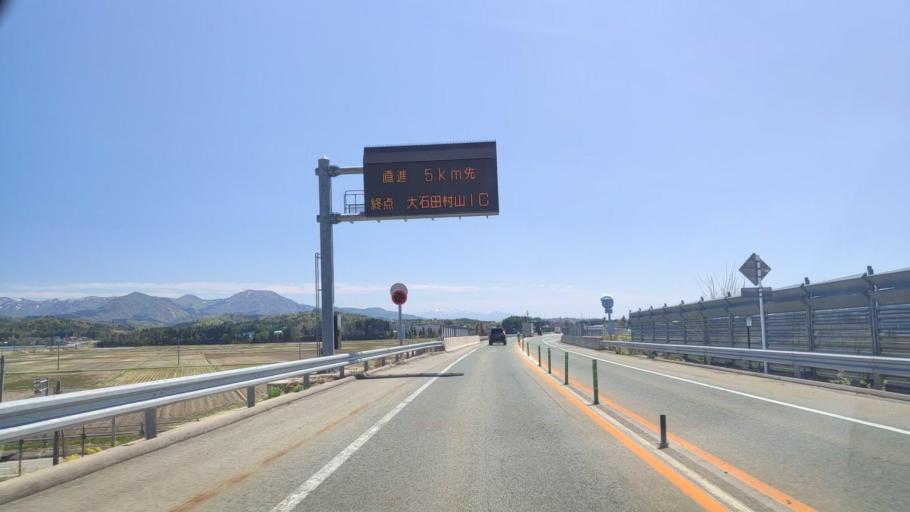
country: JP
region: Yamagata
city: Obanazawa
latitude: 38.6099
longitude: 140.3885
